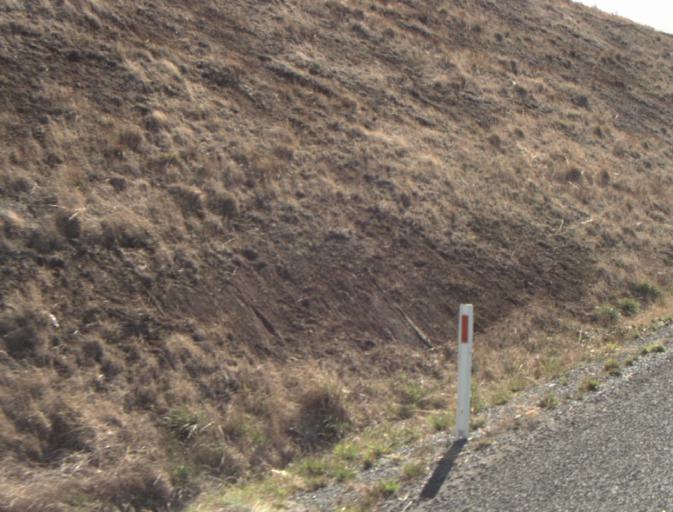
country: AU
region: Tasmania
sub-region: Launceston
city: Mayfield
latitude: -41.3559
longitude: 147.1048
